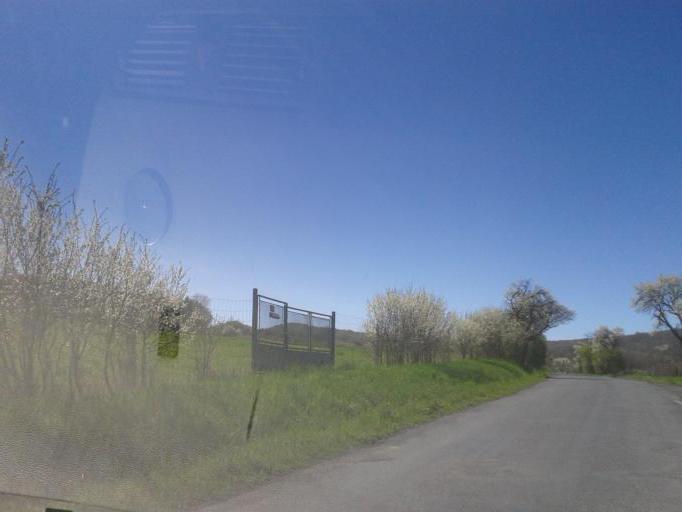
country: CZ
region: Central Bohemia
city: Revnice
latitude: 49.8933
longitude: 14.1454
